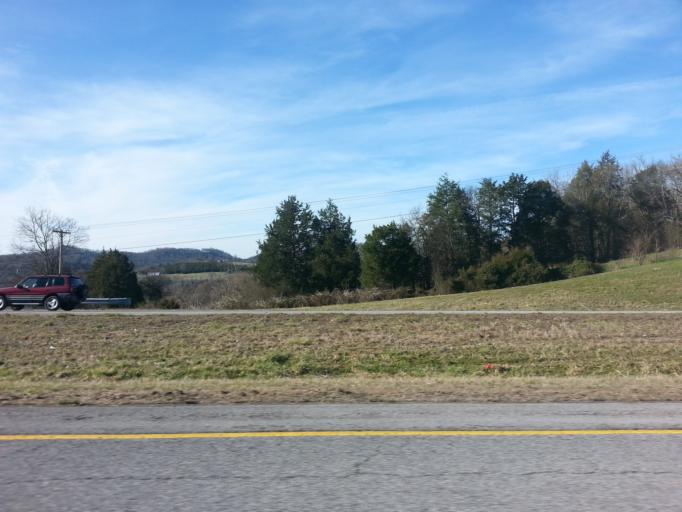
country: US
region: Tennessee
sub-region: Cannon County
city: Woodbury
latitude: 35.8174
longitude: -86.1006
